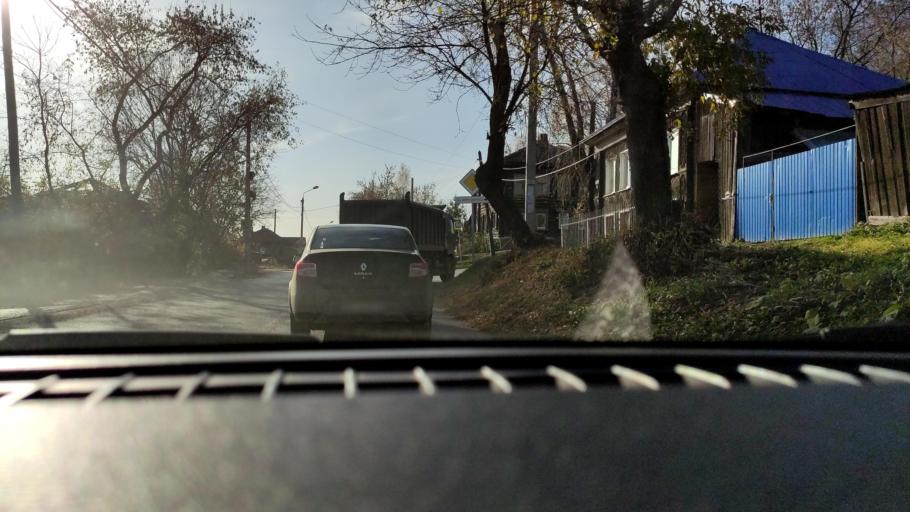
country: RU
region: Perm
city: Perm
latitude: 58.0331
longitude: 56.3129
